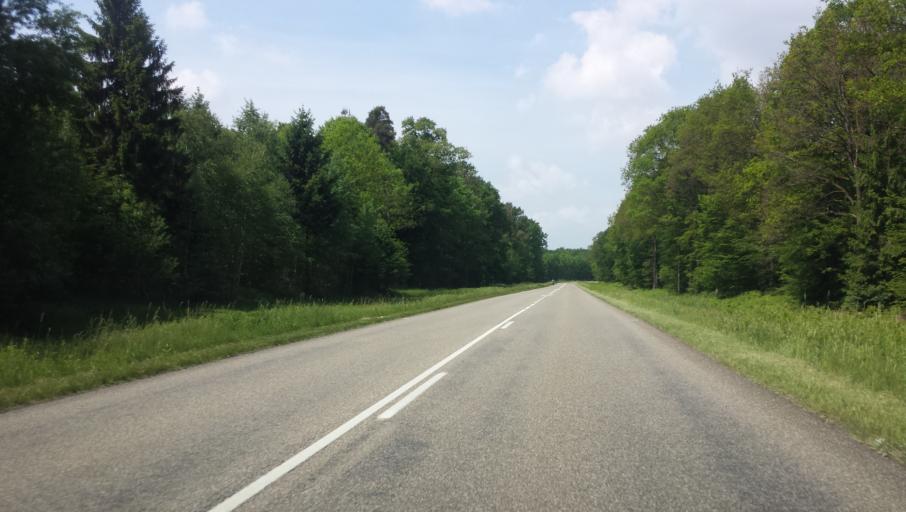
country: DE
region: Rheinland-Pfalz
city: Scheibenhardt
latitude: 48.9872
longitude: 8.0999
